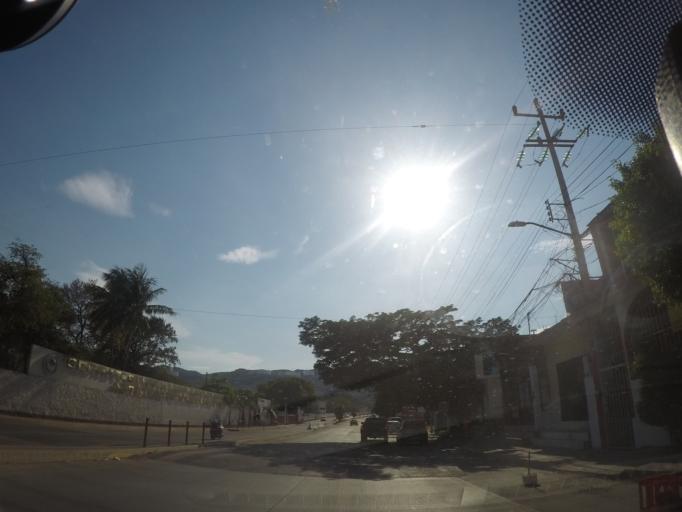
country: MX
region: Oaxaca
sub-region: Salina Cruz
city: Salina Cruz
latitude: 16.1730
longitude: -95.2011
